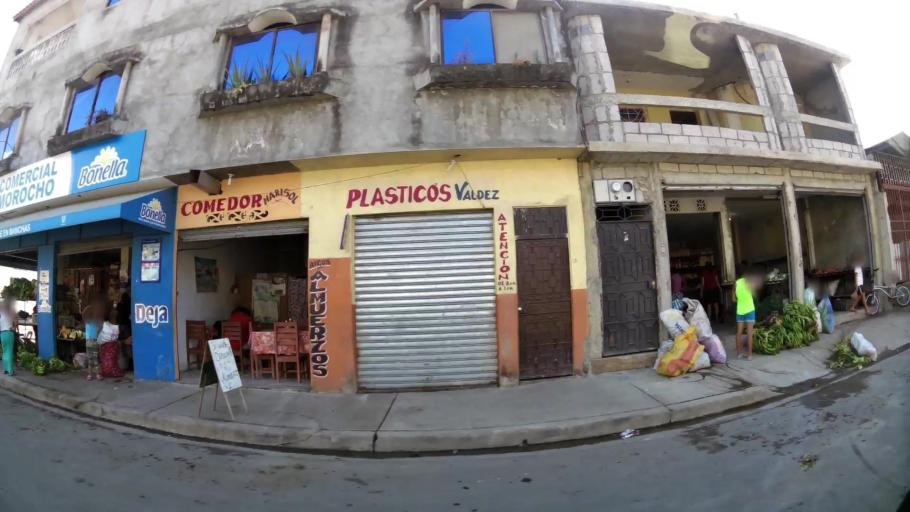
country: EC
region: Guayas
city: Eloy Alfaro
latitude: -2.0833
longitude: -79.9276
